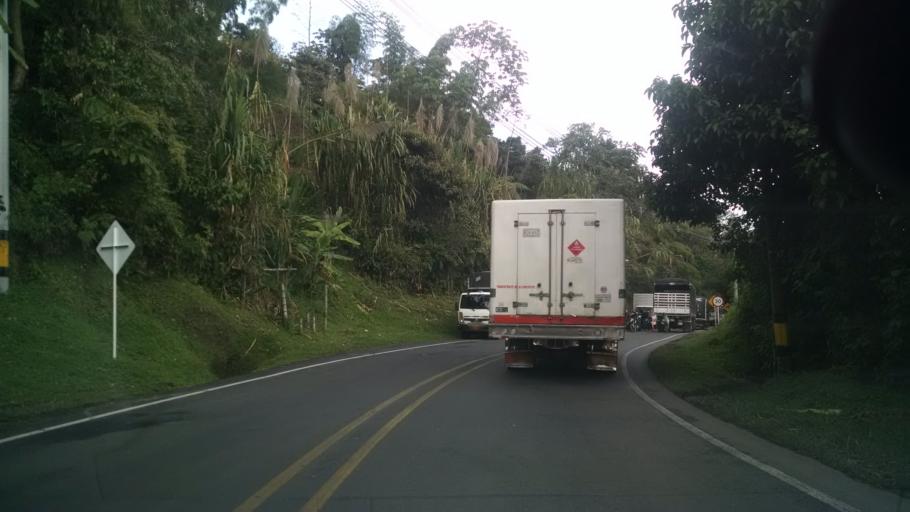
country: CO
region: Antioquia
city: Santa Barbara
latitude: 5.8846
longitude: -75.5723
